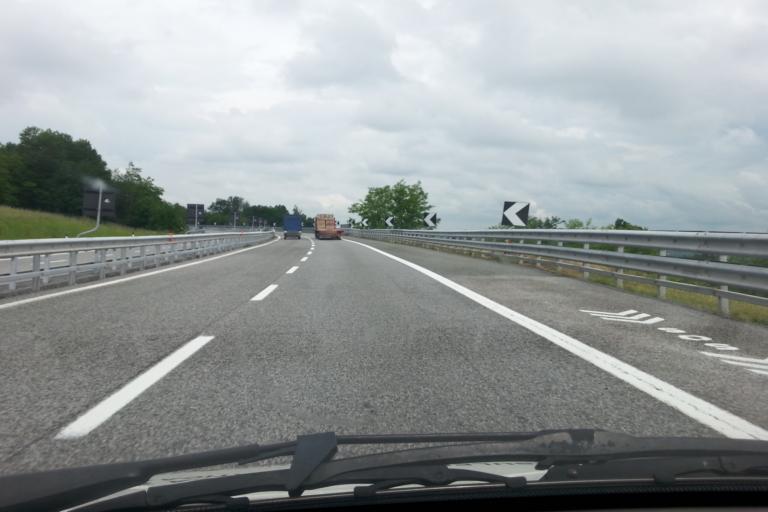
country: IT
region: Piedmont
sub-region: Provincia di Cuneo
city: Bastia Mondovi
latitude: 44.4224
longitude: 7.8879
